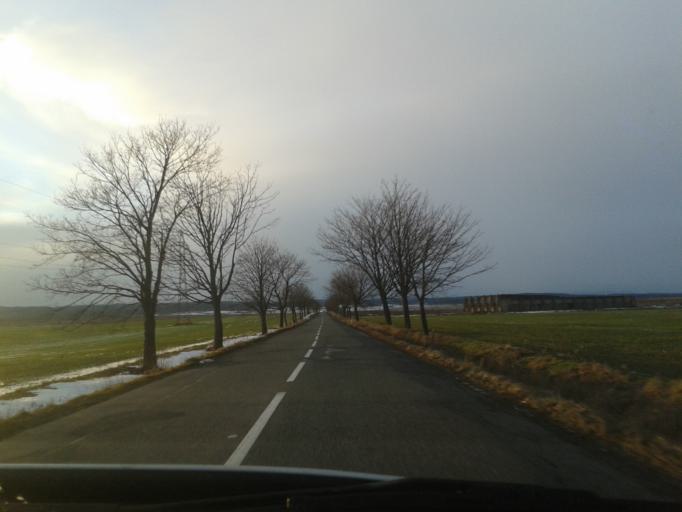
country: CZ
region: Olomoucky
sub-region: Okres Prostejov
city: Plumlov
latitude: 49.4910
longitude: 17.0003
